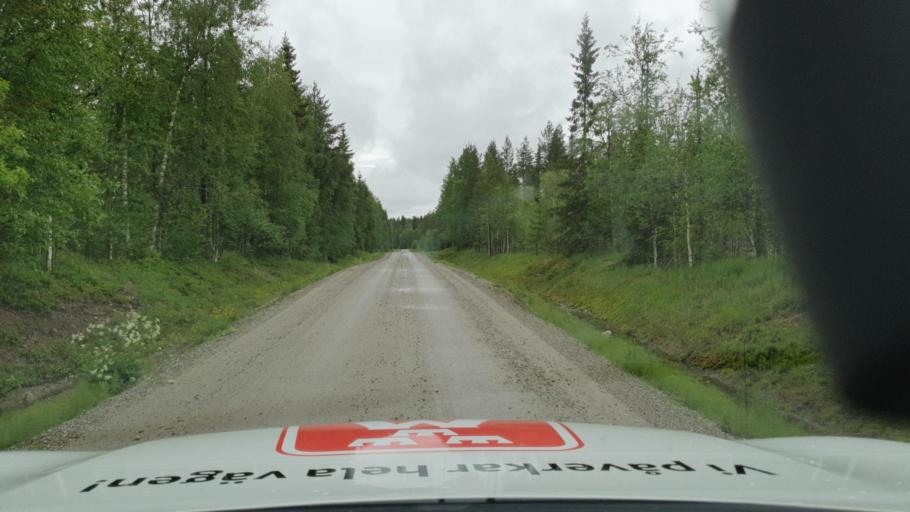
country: SE
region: Vaesterbotten
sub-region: Dorotea Kommun
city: Dorotea
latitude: 64.0077
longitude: 16.7986
